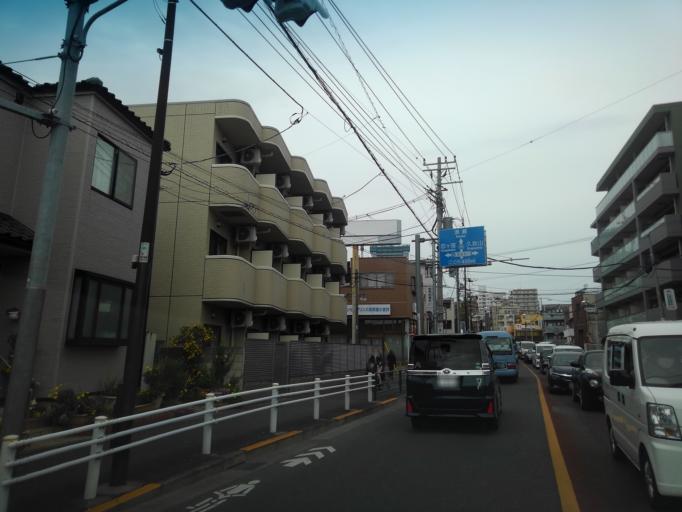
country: JP
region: Tokyo
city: Kokubunji
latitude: 35.6950
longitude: 139.5054
